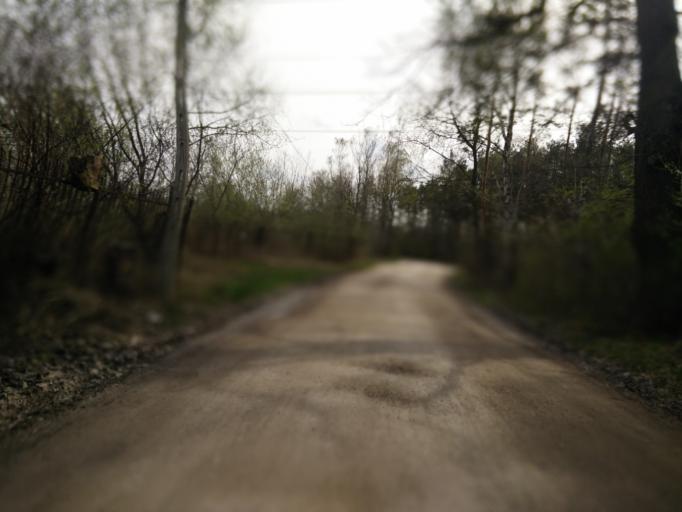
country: PL
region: Masovian Voivodeship
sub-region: Powiat warszawski zachodni
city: Izabelin
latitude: 52.2892
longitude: 20.8391
